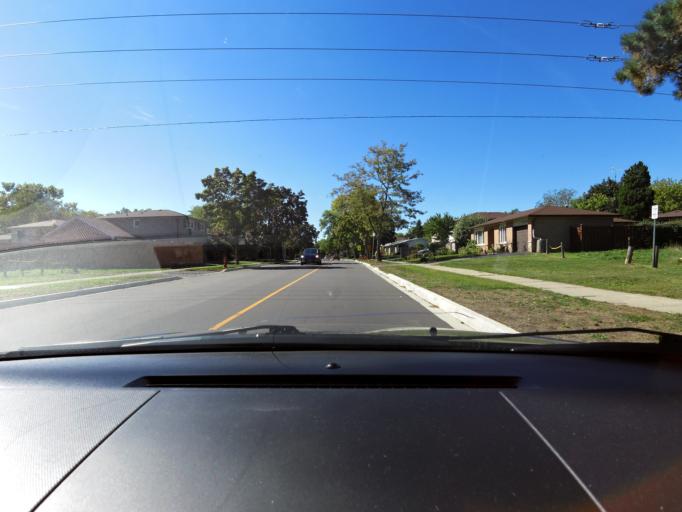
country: CA
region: Ontario
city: Burlington
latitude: 43.3690
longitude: -79.8129
